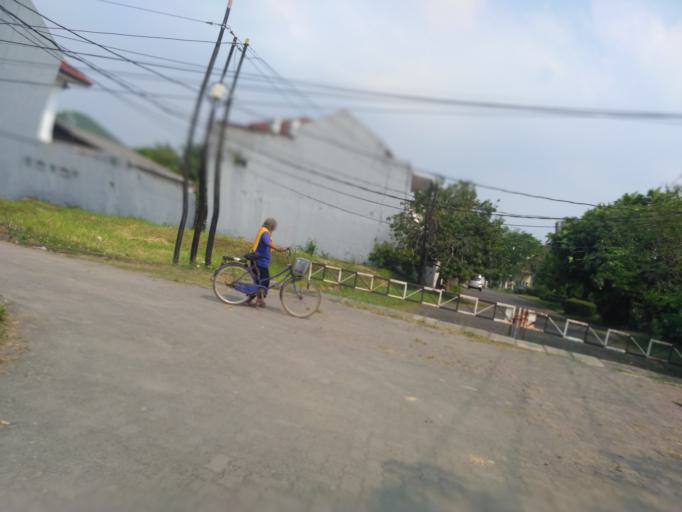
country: ID
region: Central Java
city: Semarang
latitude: -6.9657
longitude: 110.3890
